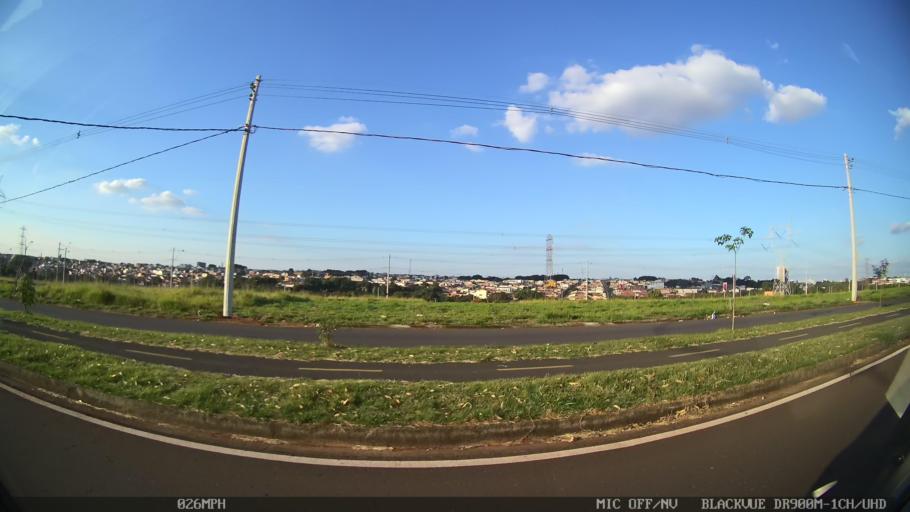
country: BR
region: Sao Paulo
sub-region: Santa Barbara D'Oeste
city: Santa Barbara d'Oeste
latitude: -22.7462
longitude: -47.3890
